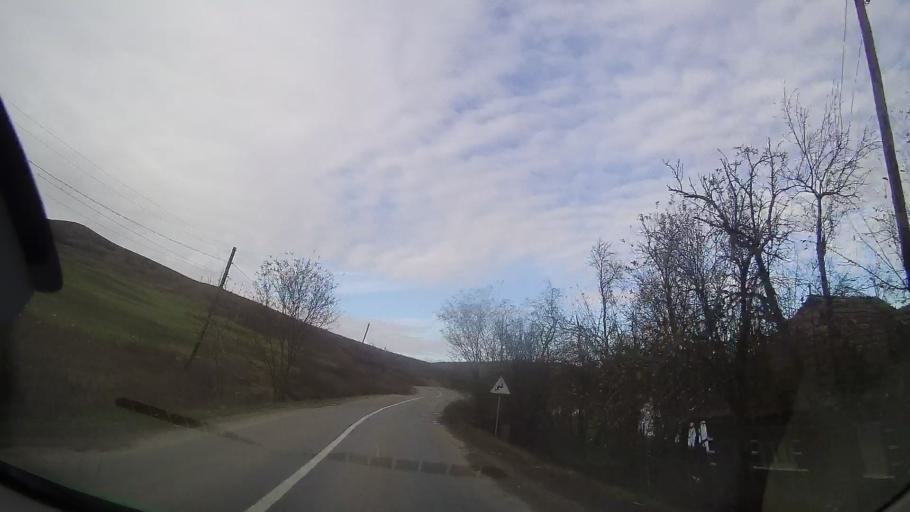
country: RO
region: Cluj
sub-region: Comuna Geaca
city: Geaca
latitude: 46.8501
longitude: 24.0936
